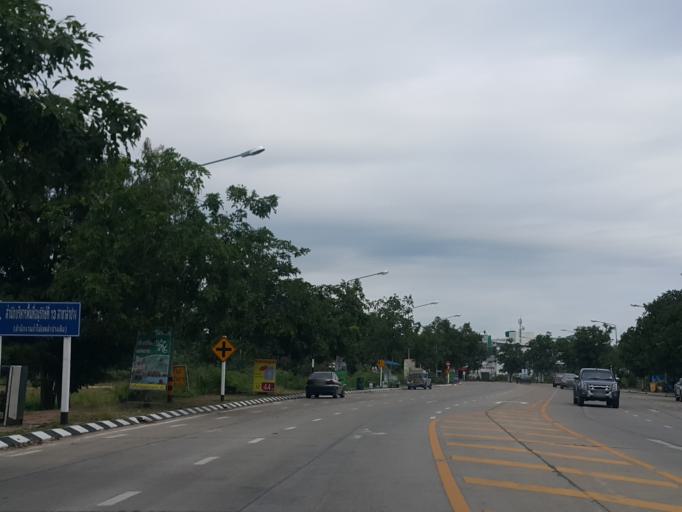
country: TH
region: Lampang
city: Lampang
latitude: 18.2868
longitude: 99.5113
